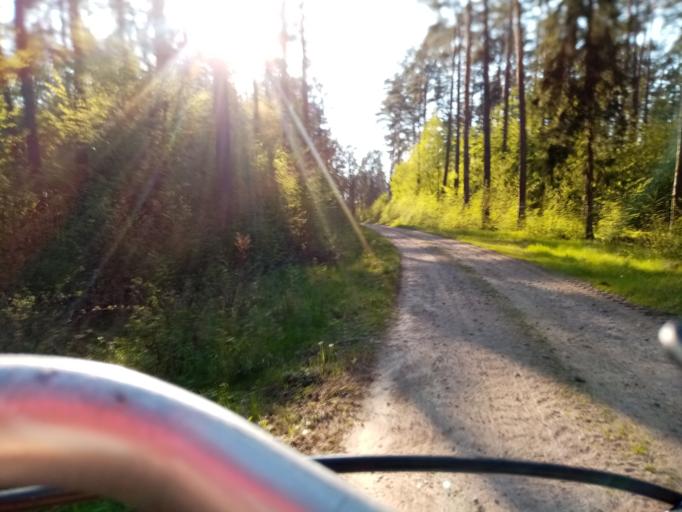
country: PL
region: Kujawsko-Pomorskie
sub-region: Powiat brodnicki
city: Gorzno
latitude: 53.1615
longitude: 19.6830
